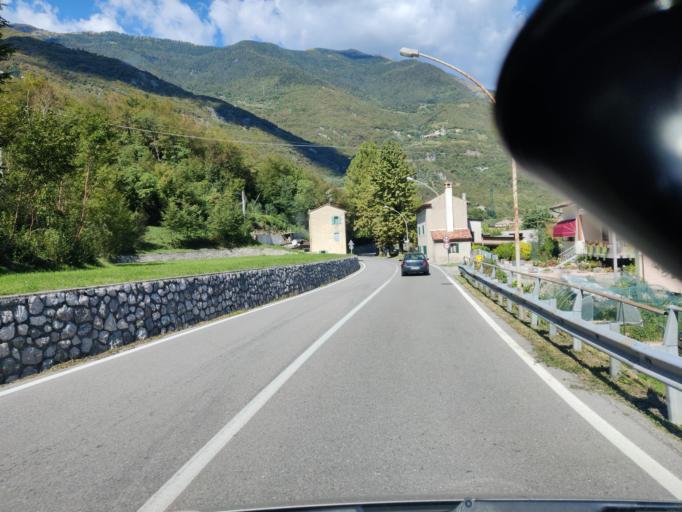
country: IT
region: Veneto
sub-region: Provincia di Treviso
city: Revine
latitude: 46.0143
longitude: 12.2891
